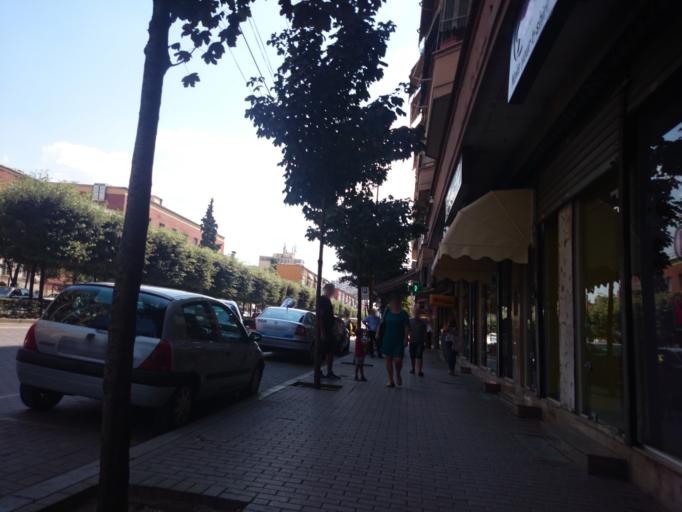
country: AL
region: Tirane
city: Tirana
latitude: 41.3352
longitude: 19.8164
